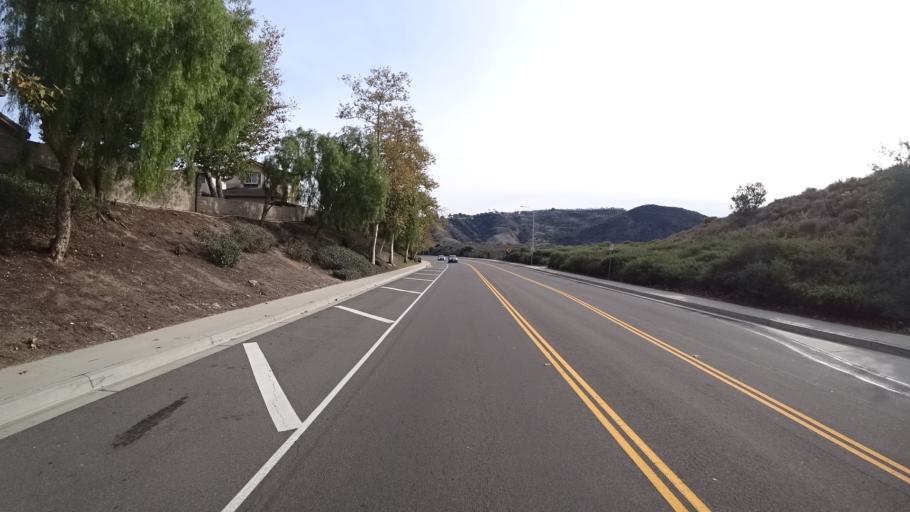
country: US
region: California
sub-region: Orange County
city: Aliso Viejo
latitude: 33.5511
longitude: -117.7296
